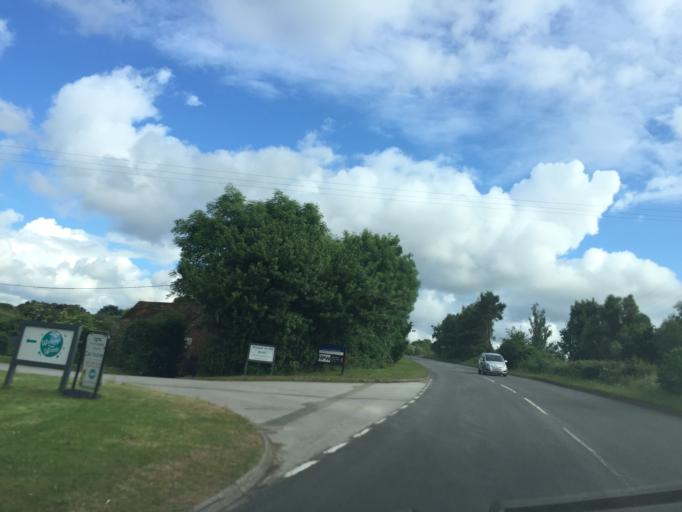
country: GB
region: England
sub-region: Hampshire
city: Cadnam
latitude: 50.9464
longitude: -1.5387
